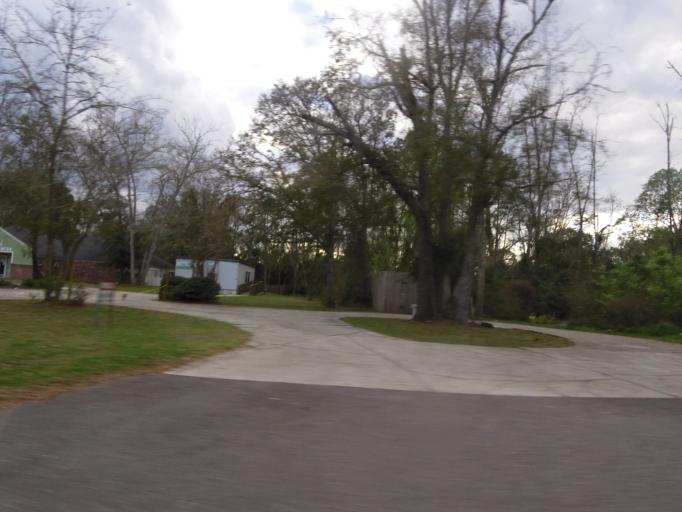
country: US
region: Florida
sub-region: Saint Johns County
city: Fruit Cove
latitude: 30.2030
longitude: -81.5834
